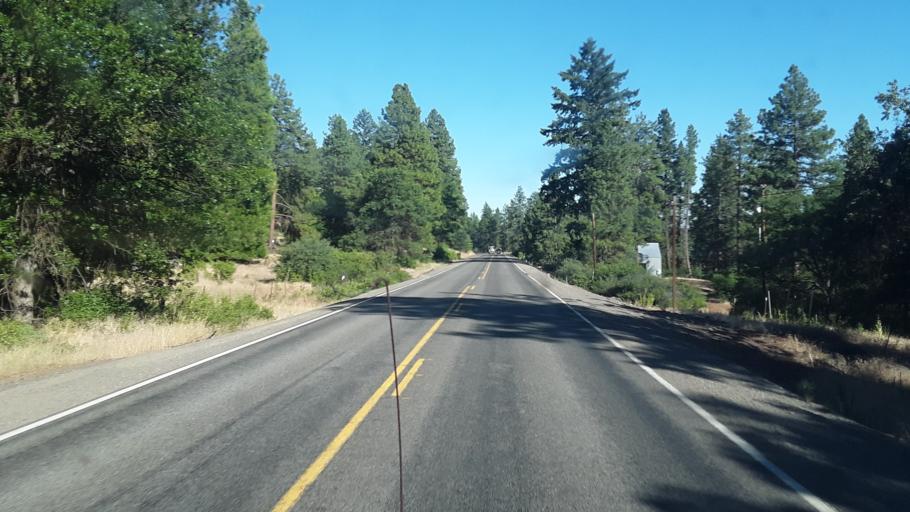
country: US
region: Oregon
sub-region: Klamath County
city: Klamath Falls
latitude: 42.2787
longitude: -121.9120
